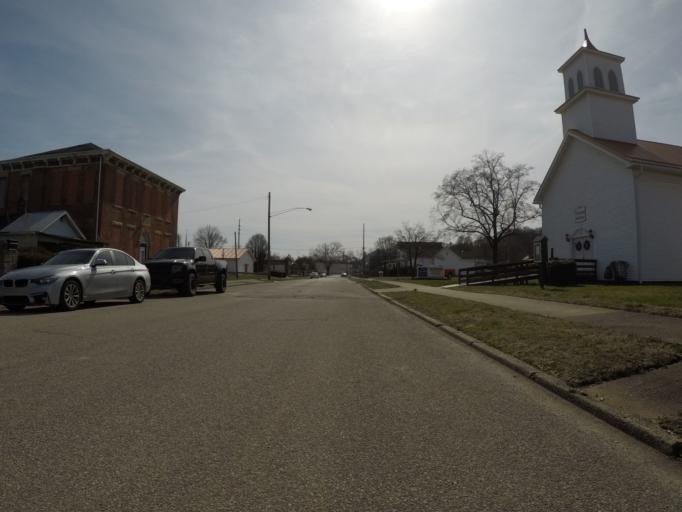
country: US
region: West Virginia
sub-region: Cabell County
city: Huntington
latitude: 38.4288
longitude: -82.3875
